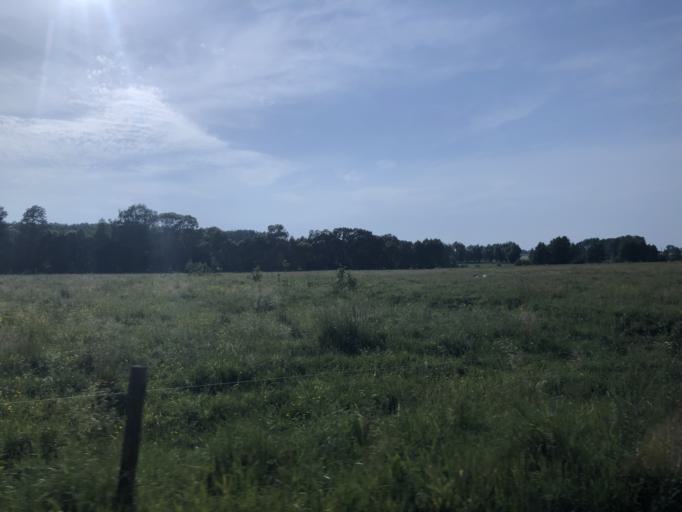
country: PL
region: Podlasie
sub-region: Lomza
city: Lomza
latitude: 53.1453
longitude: 22.0158
